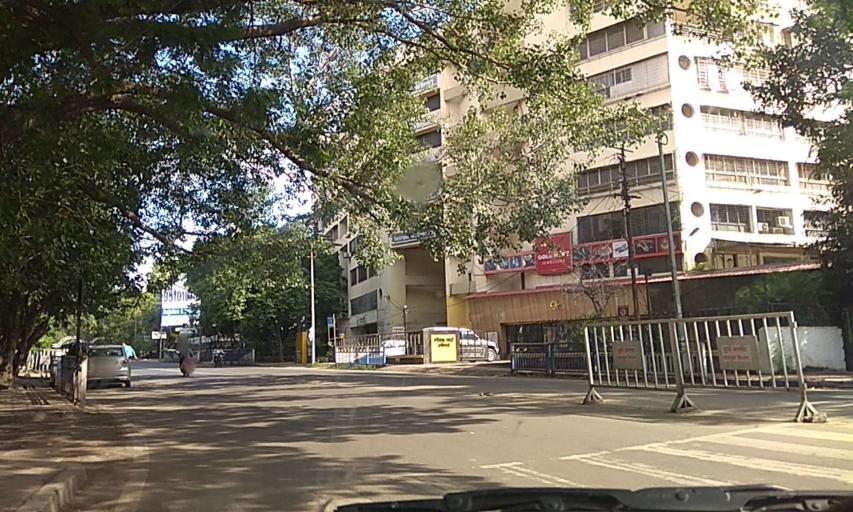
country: IN
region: Maharashtra
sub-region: Pune Division
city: Pune
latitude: 18.5249
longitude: 73.8769
